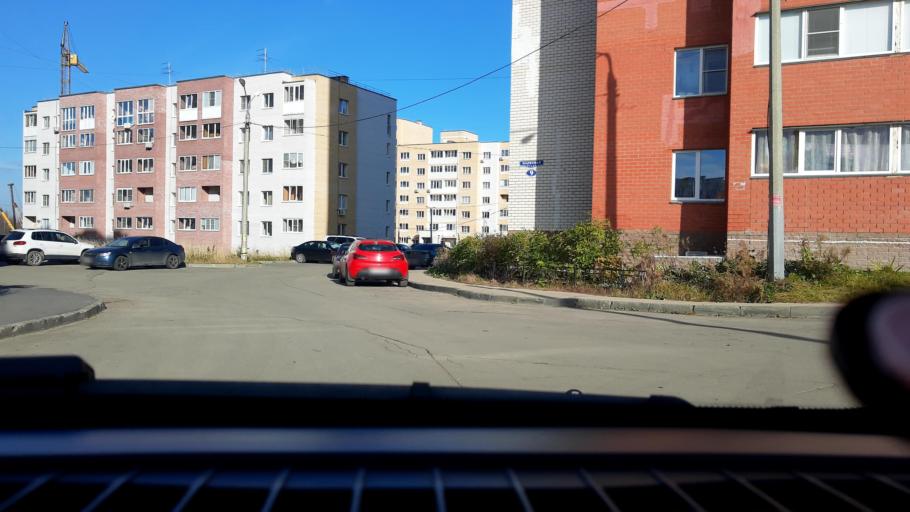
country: RU
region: Nizjnij Novgorod
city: Kstovo
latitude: 56.1597
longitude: 44.2149
